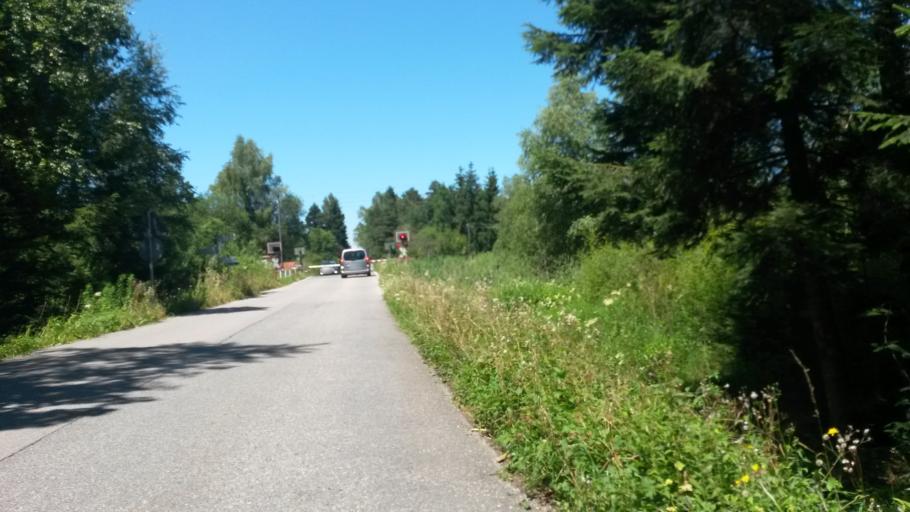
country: DE
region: Bavaria
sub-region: Upper Bavaria
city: Bernau am Chiemsee
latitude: 47.8134
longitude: 12.3975
